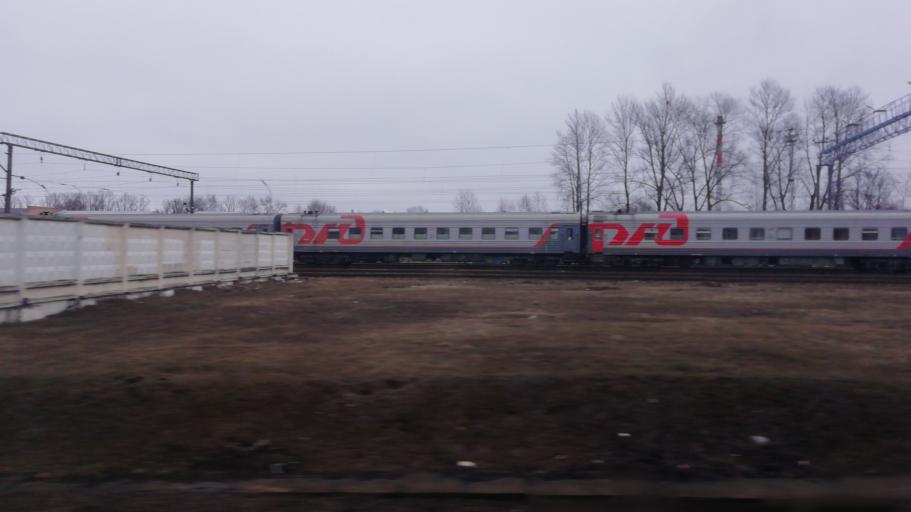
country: RU
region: St.-Petersburg
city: Kupchino
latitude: 59.8844
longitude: 30.3463
